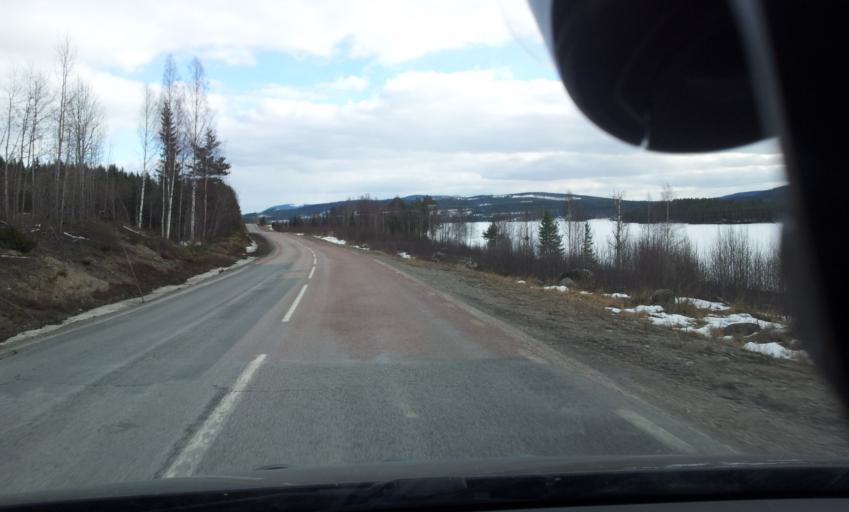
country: SE
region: Gaevleborg
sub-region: Ljusdals Kommun
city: Farila
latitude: 62.1387
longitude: 15.6891
